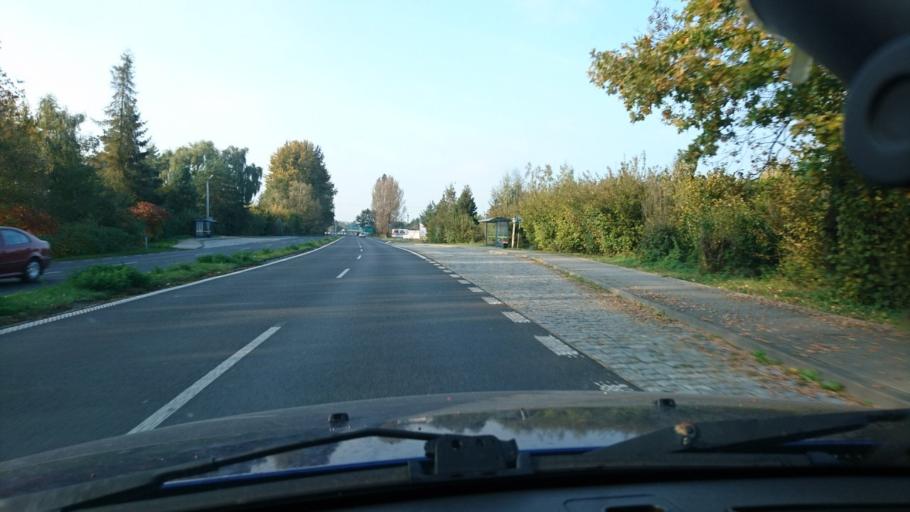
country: PL
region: Silesian Voivodeship
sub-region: Powiat cieszynski
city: Gorki Wielkie
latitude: 49.7786
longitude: 18.8085
